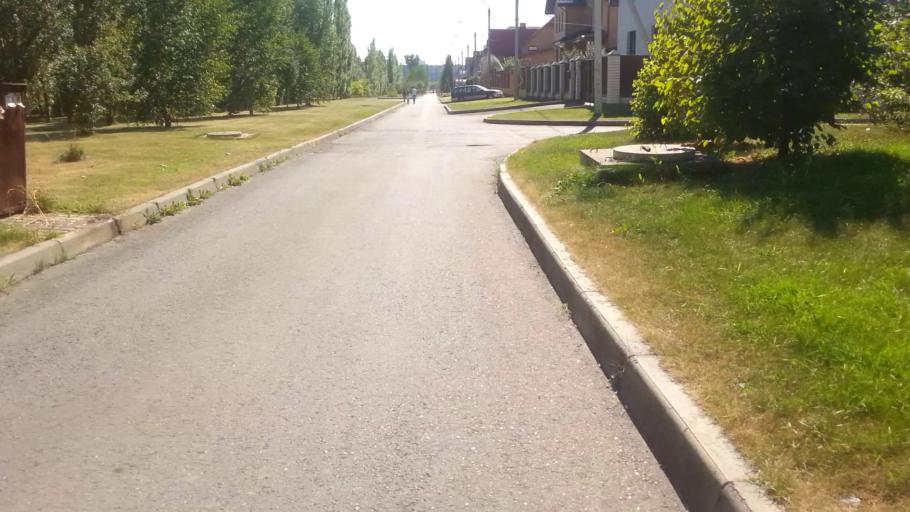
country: RU
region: Altai Krai
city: Novosilikatnyy
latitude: 53.3548
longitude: 83.6562
